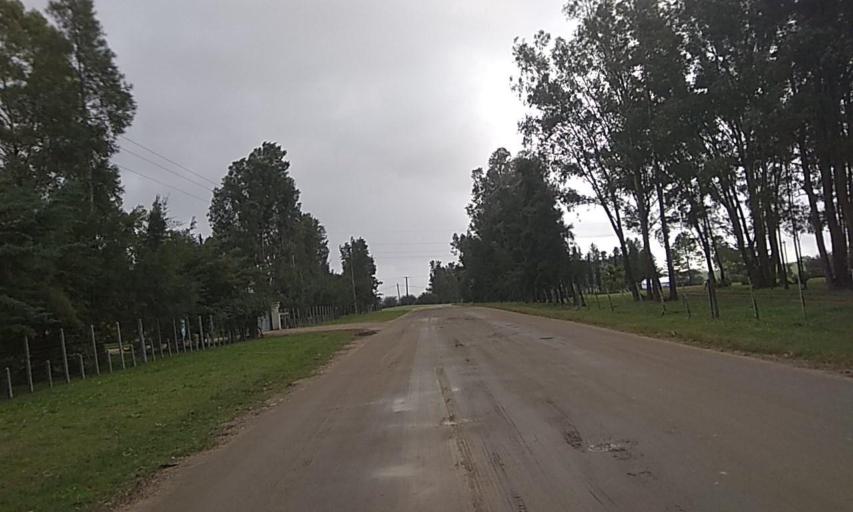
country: UY
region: Florida
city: Florida
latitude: -34.0940
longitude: -56.1694
